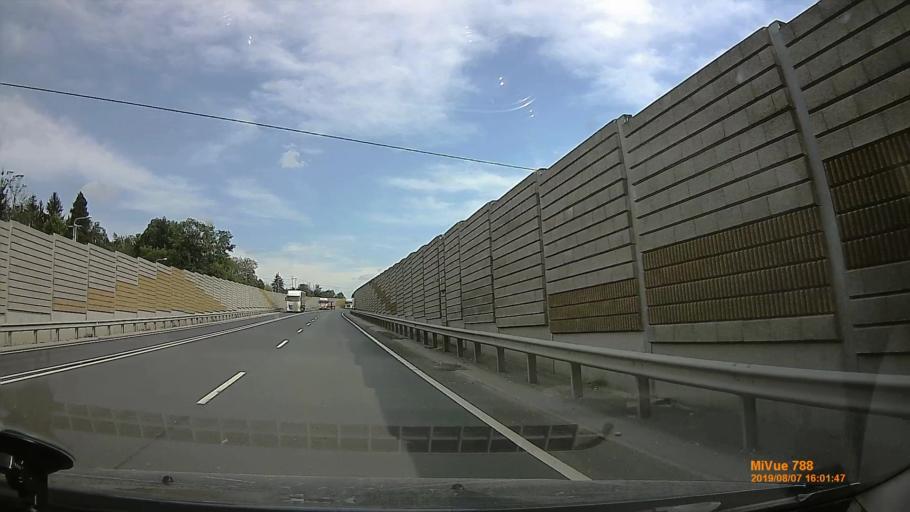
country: HU
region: Vas
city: Kormend
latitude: 46.9861
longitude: 16.6210
